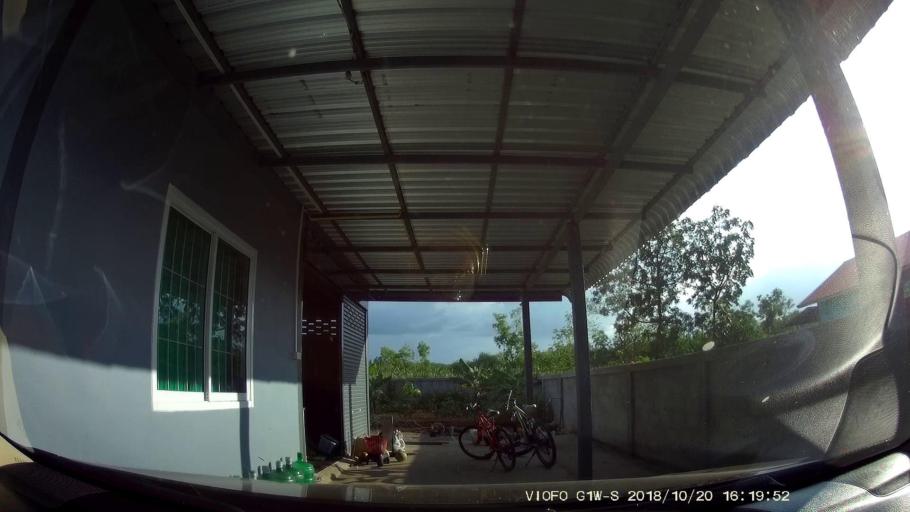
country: TH
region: Khon Kaen
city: Chum Phae
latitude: 16.4896
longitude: 102.1166
